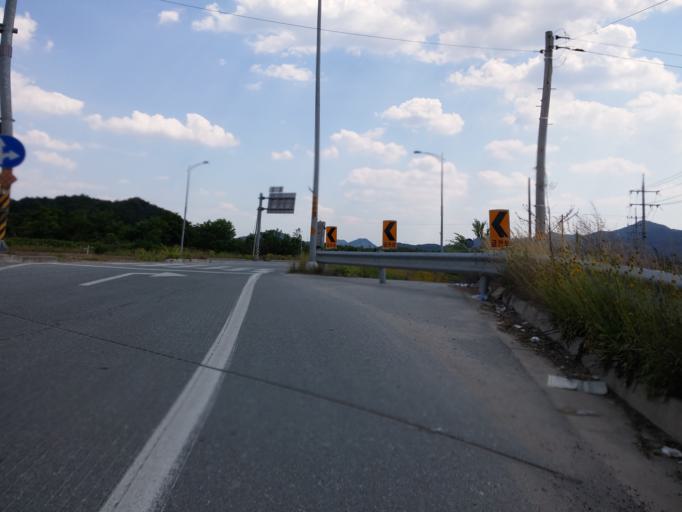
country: KR
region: Chungcheongbuk-do
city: Cheongju-si
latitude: 36.5613
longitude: 127.5067
